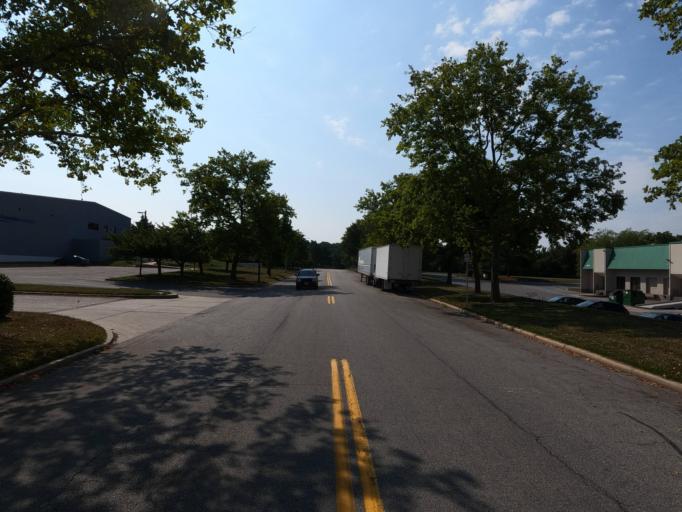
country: US
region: Maryland
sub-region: Howard County
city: Savage
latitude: 39.1711
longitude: -76.8395
